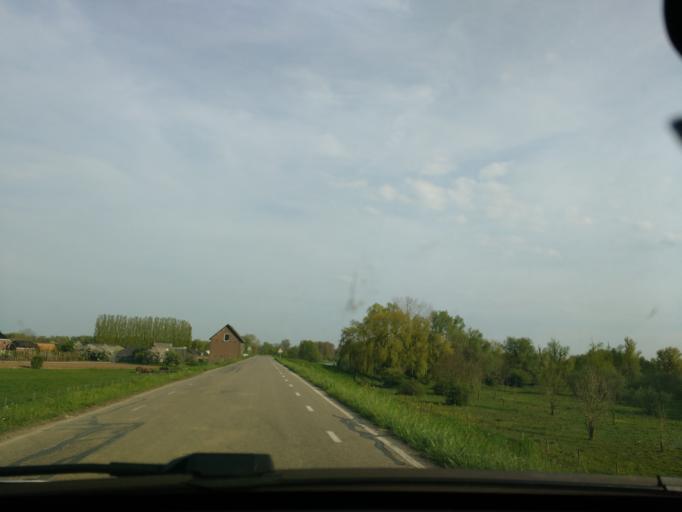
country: NL
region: Utrecht
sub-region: Gemeente Rhenen
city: Rhenen
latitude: 51.9522
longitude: 5.6127
